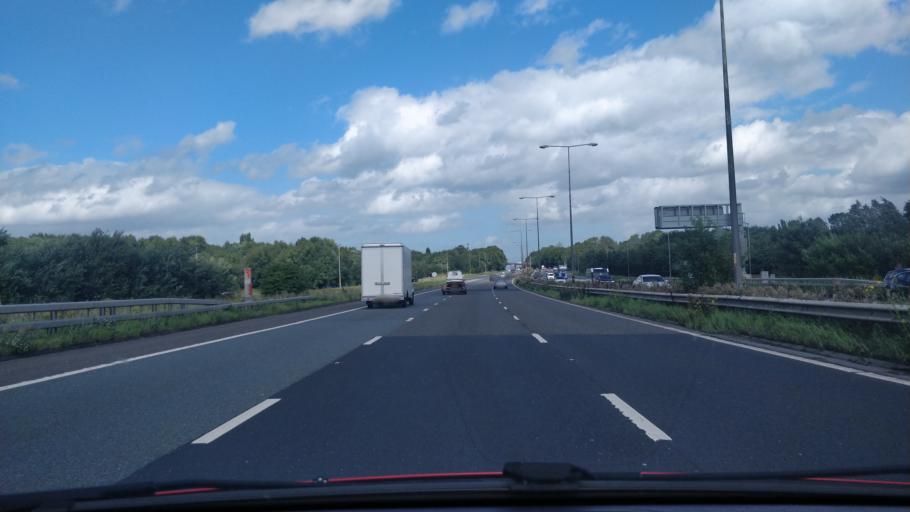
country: GB
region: England
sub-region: St. Helens
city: Billinge
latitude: 53.5320
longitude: -2.6986
